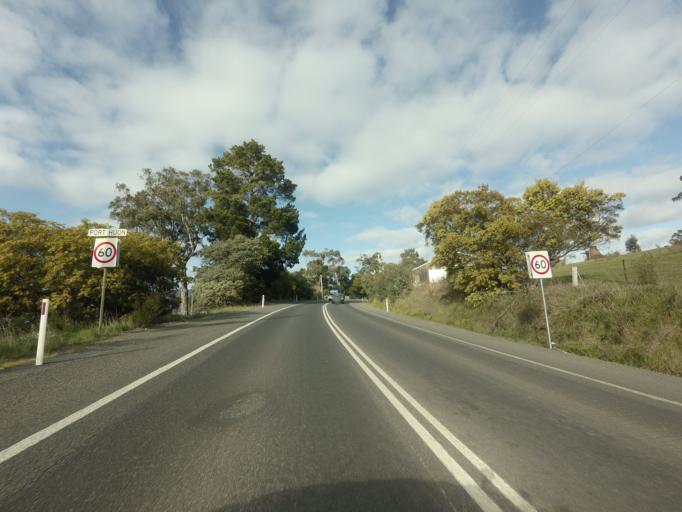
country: AU
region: Tasmania
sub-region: Huon Valley
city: Geeveston
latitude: -43.1575
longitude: 146.9798
